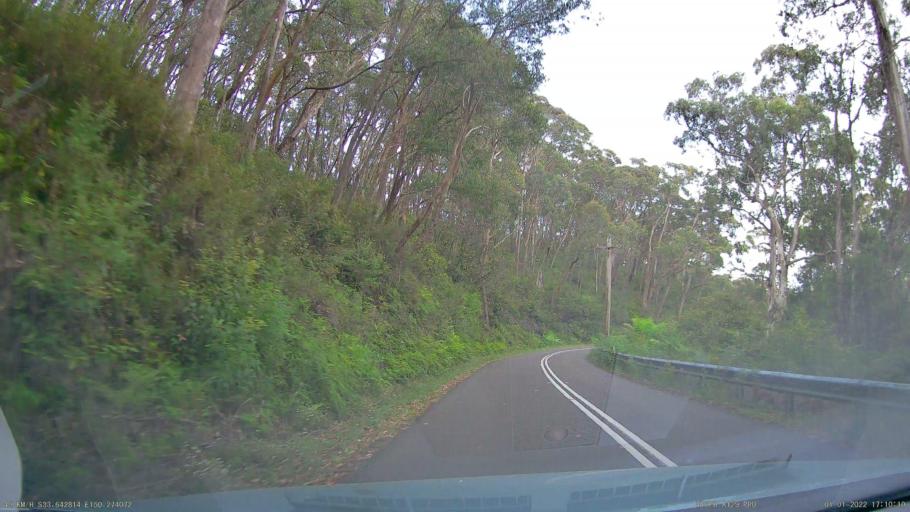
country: AU
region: New South Wales
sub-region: Blue Mountains Municipality
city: Blackheath
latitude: -33.6427
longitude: 150.2741
